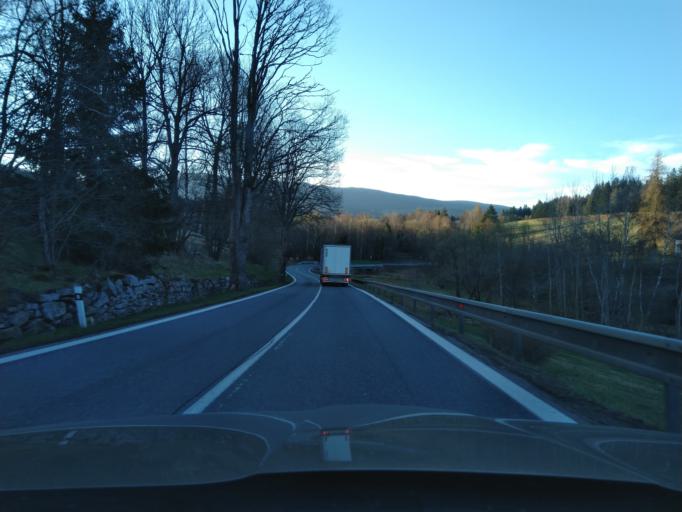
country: CZ
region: Jihocesky
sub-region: Okres Prachatice
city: Vimperk
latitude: 49.0267
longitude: 13.7655
